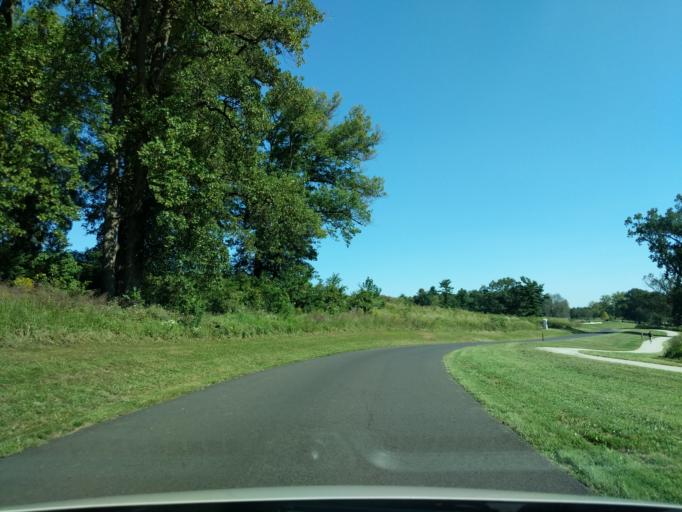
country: US
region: Pennsylvania
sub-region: Chester County
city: Chesterbrook
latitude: 40.1005
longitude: -75.4495
